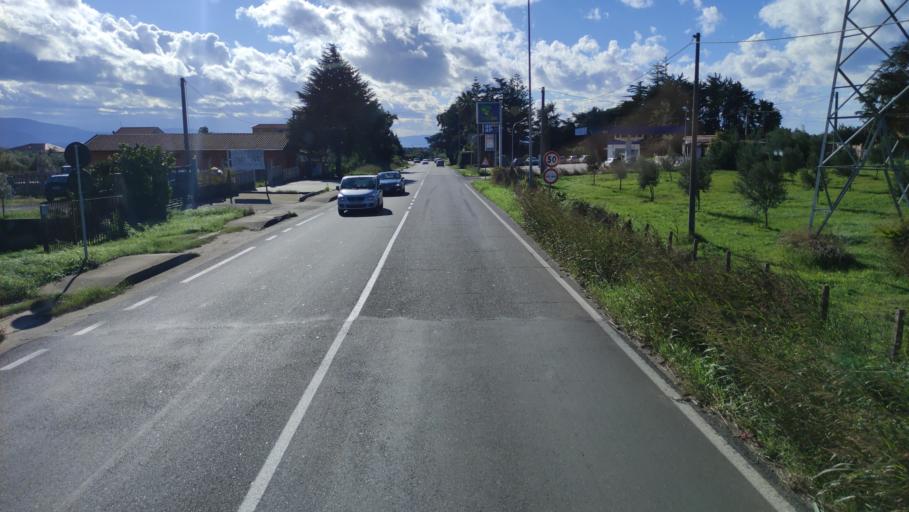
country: IT
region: Calabria
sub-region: Provincia di Catanzaro
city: Santa Eufemia Lamezia
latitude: 38.9323
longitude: 16.2868
